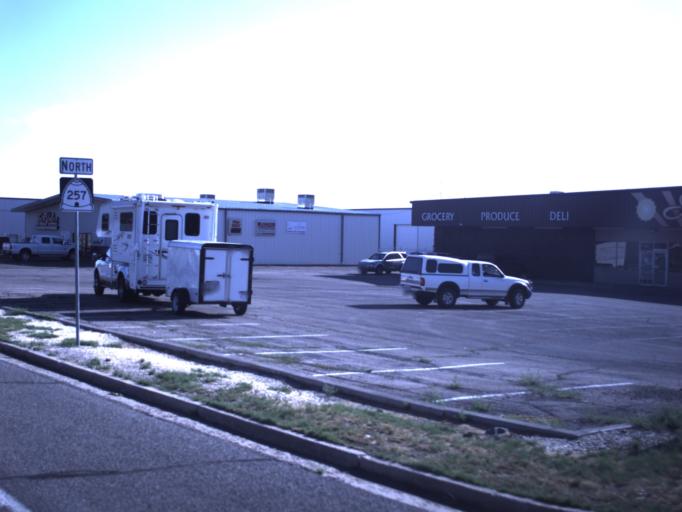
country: US
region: Utah
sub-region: Beaver County
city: Milford
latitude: 38.4030
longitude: -113.0098
